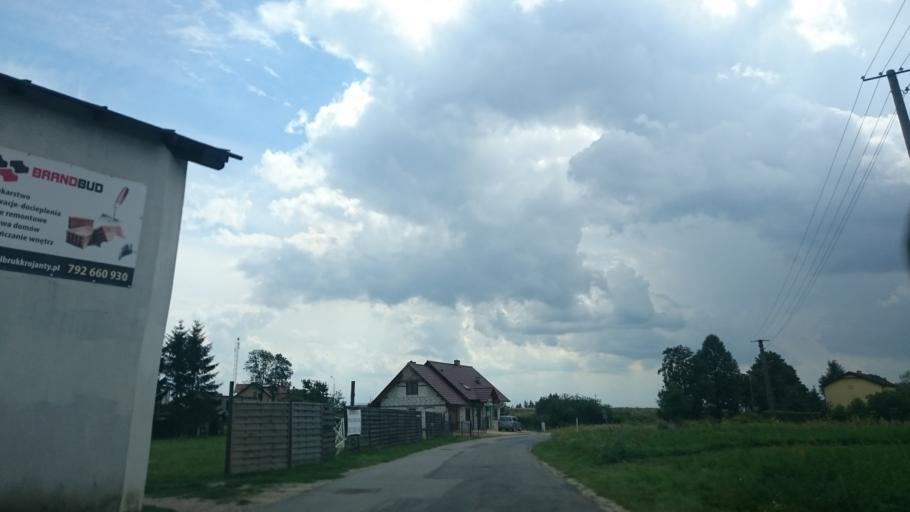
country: PL
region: Pomeranian Voivodeship
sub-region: Powiat chojnicki
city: Chojnice
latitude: 53.6990
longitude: 17.6855
